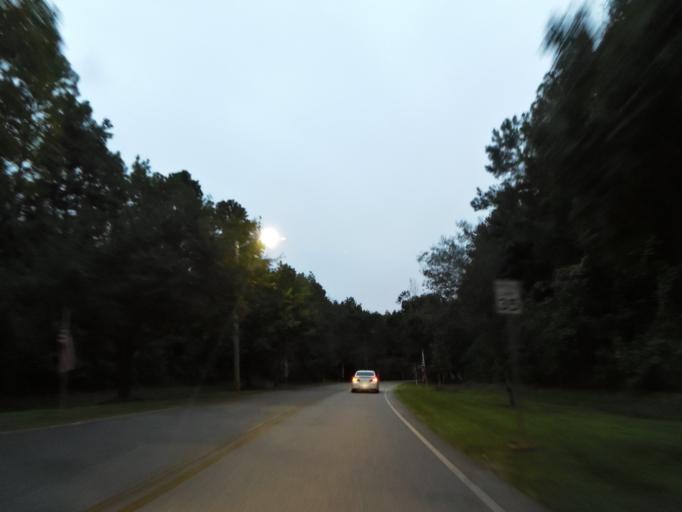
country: US
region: Alabama
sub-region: Baldwin County
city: Fairhope
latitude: 30.5494
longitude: -87.8921
